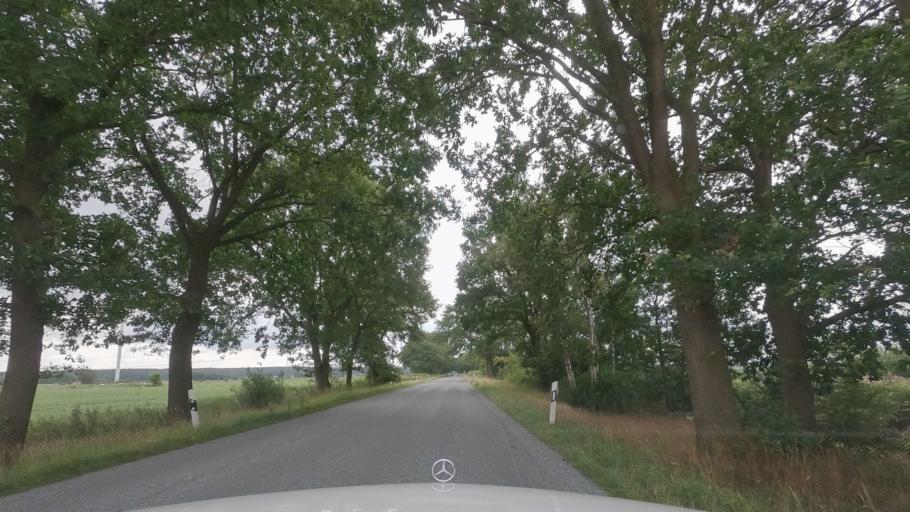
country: DE
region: Lower Saxony
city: Uthlede
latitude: 53.3018
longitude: 8.5904
